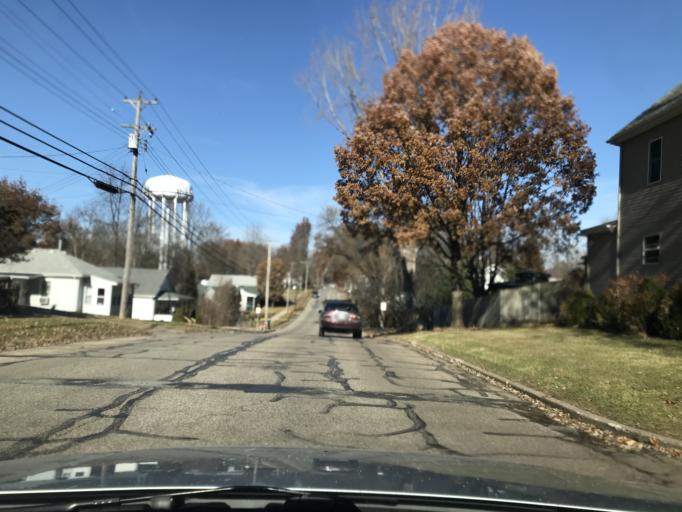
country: US
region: Illinois
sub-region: McDonough County
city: Macomb
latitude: 40.4510
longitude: -90.6673
